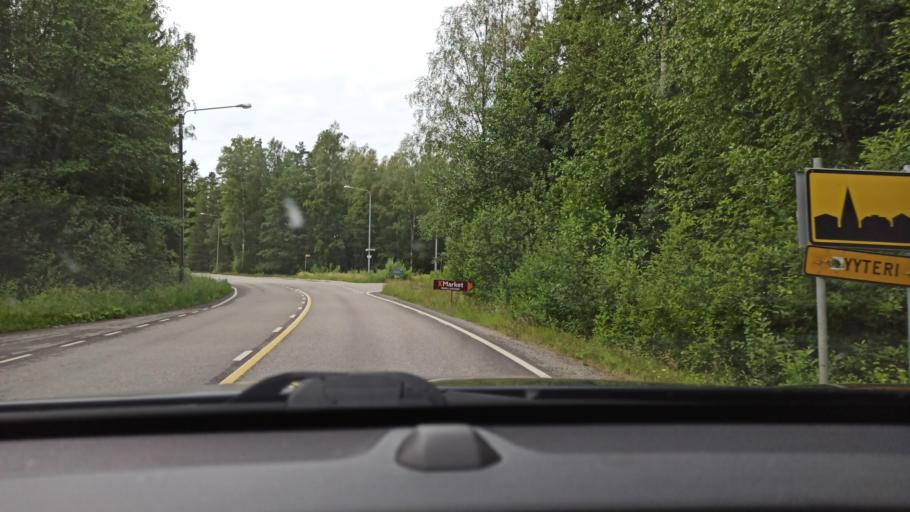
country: FI
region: Satakunta
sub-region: Pori
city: Luvia
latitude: 61.5741
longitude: 21.5430
